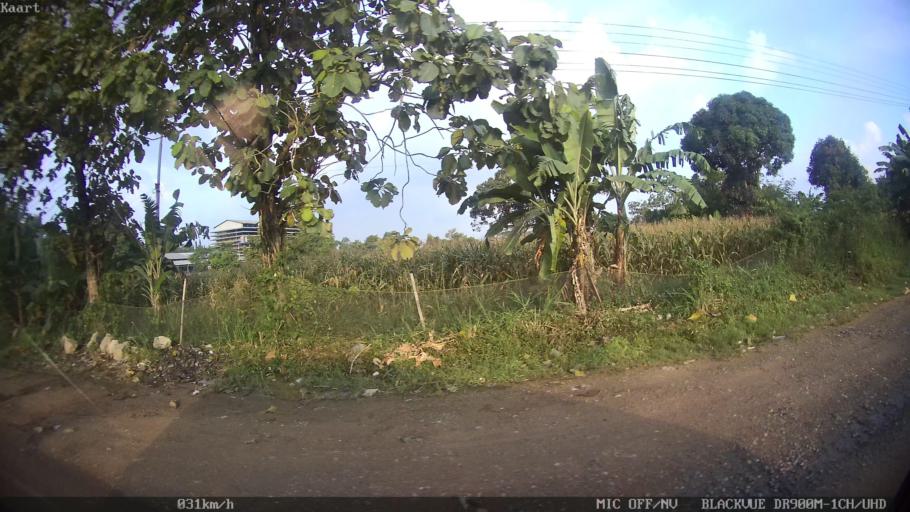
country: ID
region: Lampung
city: Panjang
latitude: -5.4118
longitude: 105.3468
